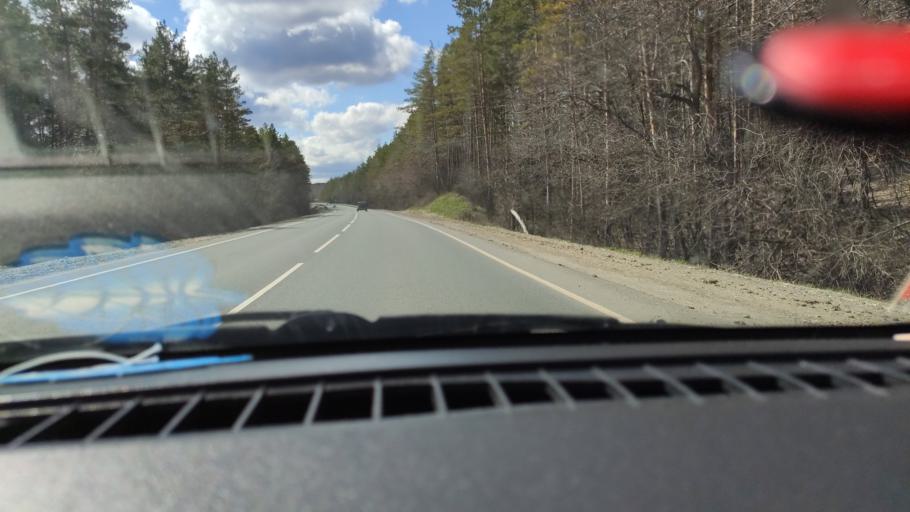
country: RU
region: Saratov
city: Khvalynsk
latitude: 52.5167
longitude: 48.0174
